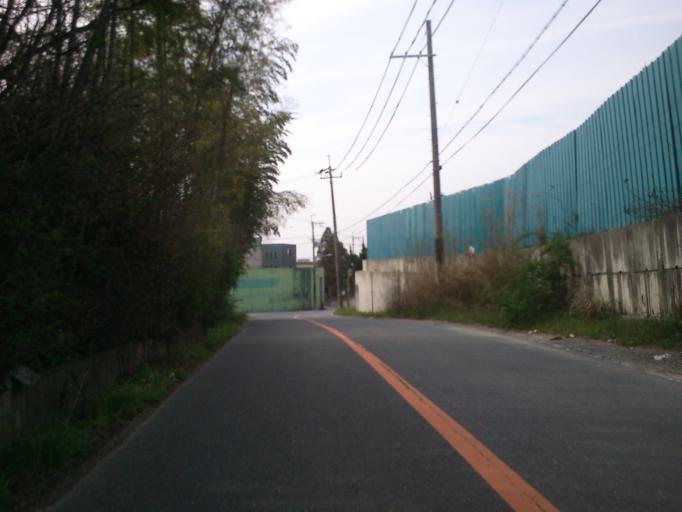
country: JP
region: Kyoto
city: Tanabe
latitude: 34.7942
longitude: 135.7425
